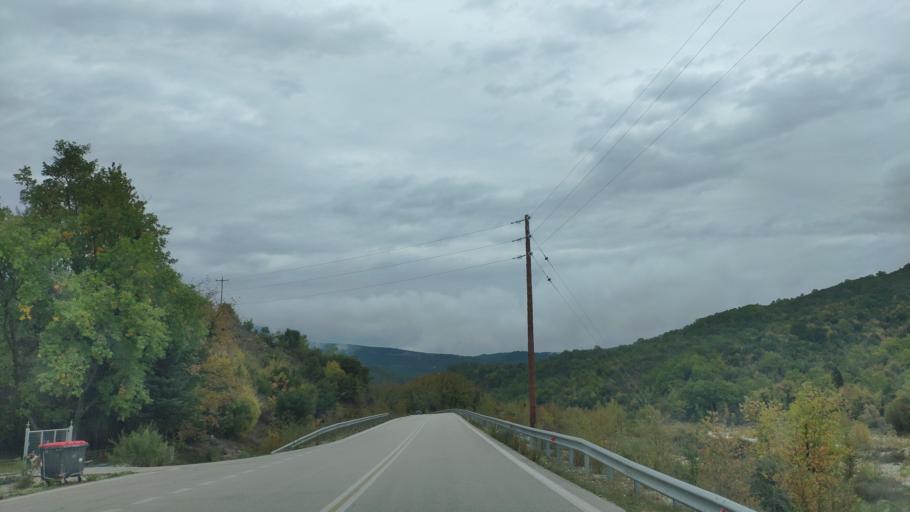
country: GR
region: Epirus
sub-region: Nomos Ioanninon
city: Pedini
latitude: 39.5253
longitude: 20.6935
